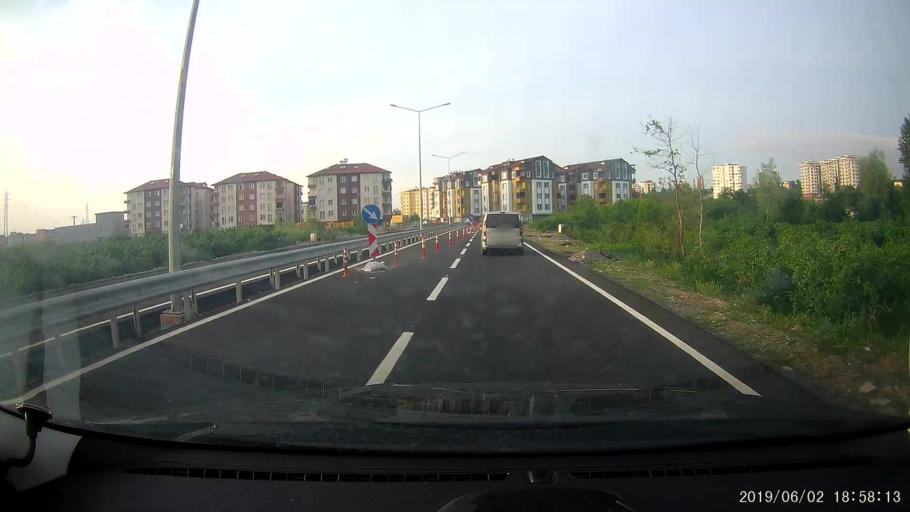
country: TR
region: Ordu
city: Ordu
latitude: 40.9601
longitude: 37.9068
